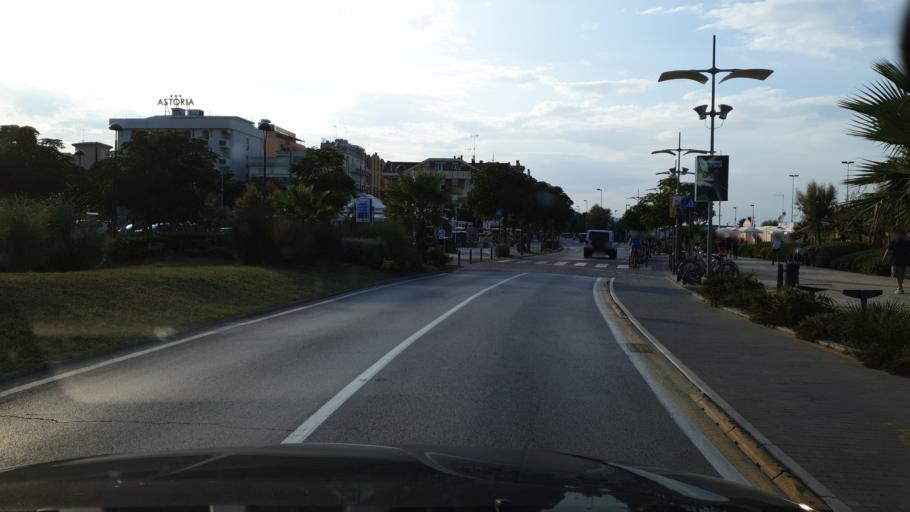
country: IT
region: Emilia-Romagna
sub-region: Provincia di Rimini
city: Misano Adriatico
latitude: 43.9840
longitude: 12.6917
